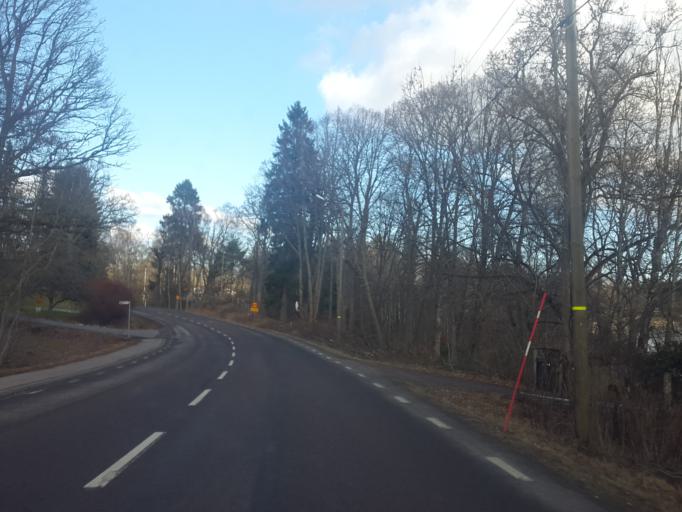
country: SE
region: Vaestra Goetaland
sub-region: Lerums Kommun
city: Grabo
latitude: 57.8765
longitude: 12.3292
